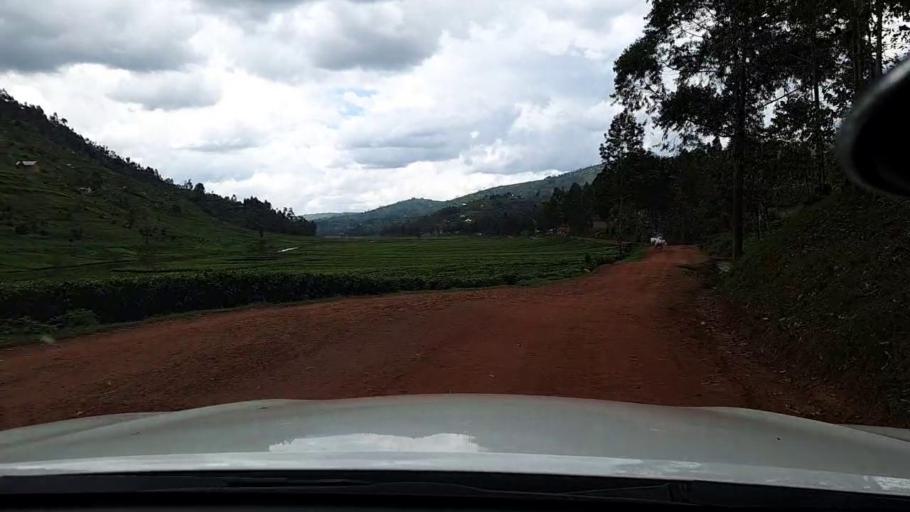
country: RW
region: Northern Province
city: Byumba
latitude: -1.6635
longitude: 29.9176
